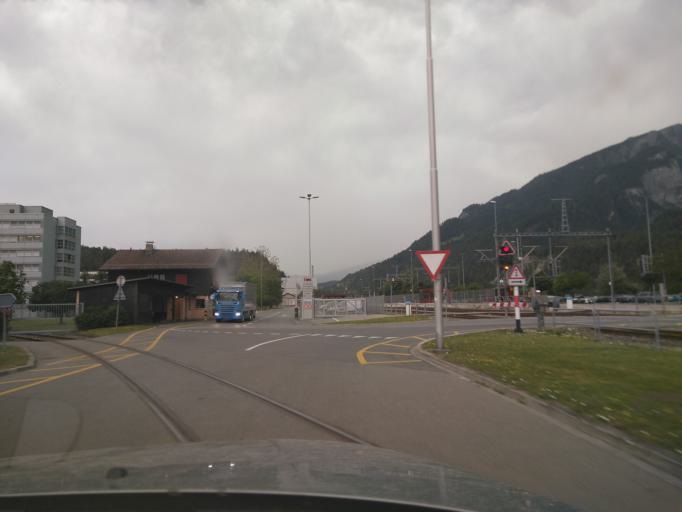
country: CH
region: Grisons
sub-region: Imboden District
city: Domat
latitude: 46.8285
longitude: 9.4316
